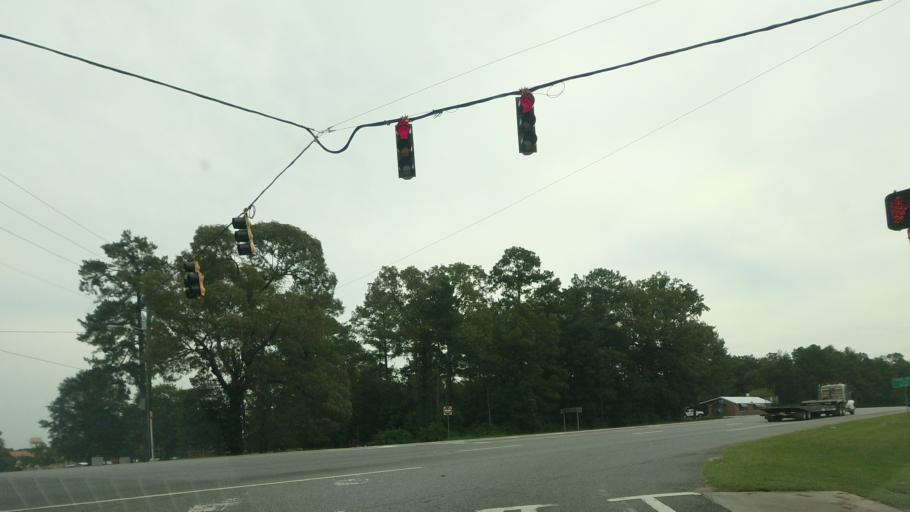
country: US
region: Georgia
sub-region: Houston County
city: Robins Air Force Base
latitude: 32.5897
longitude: -83.5890
